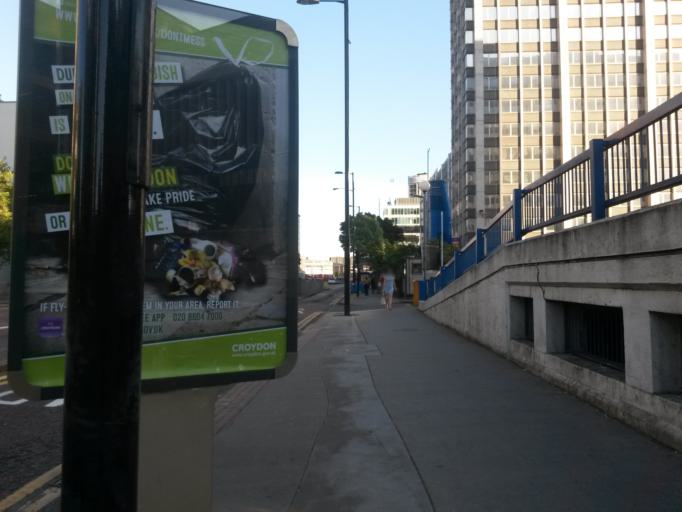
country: GB
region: England
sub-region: Greater London
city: Croydon
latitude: 51.3772
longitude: -0.0992
